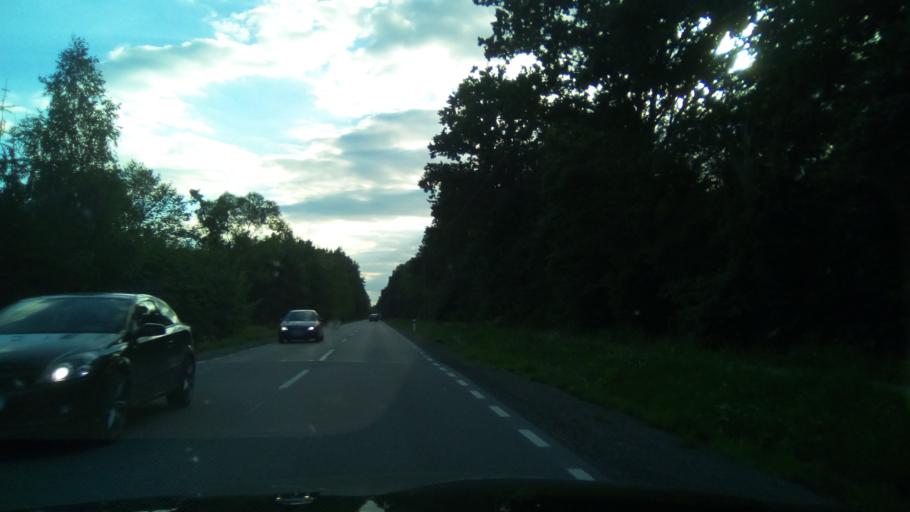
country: PL
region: Masovian Voivodeship
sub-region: Powiat bialobrzeski
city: Bialobrzegi
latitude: 51.6516
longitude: 20.9896
